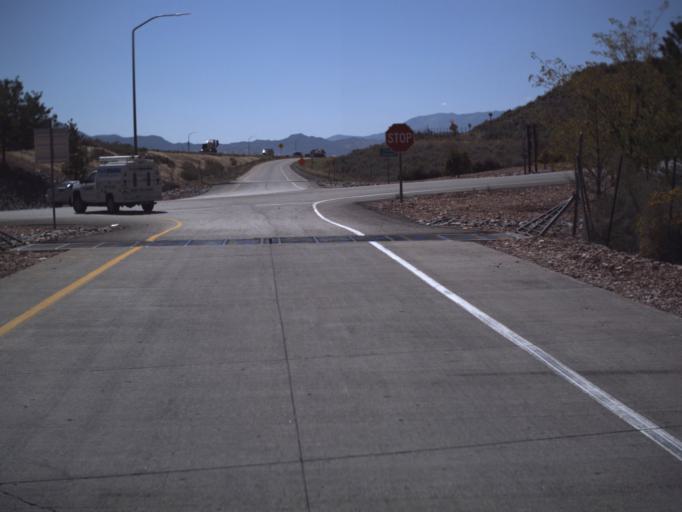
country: US
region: Utah
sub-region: Sevier County
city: Richfield
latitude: 38.7507
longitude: -112.1063
